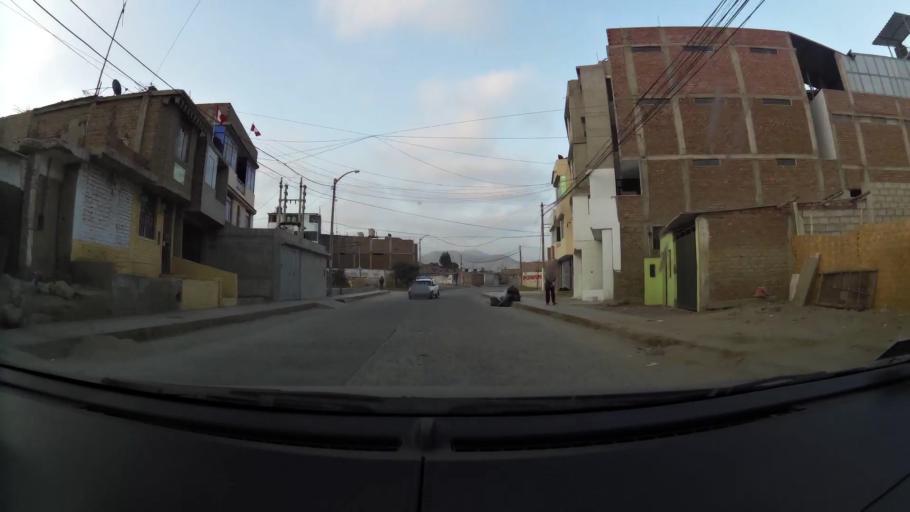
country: PE
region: La Libertad
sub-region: Provincia de Trujillo
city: El Porvenir
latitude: -8.0797
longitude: -79.0064
